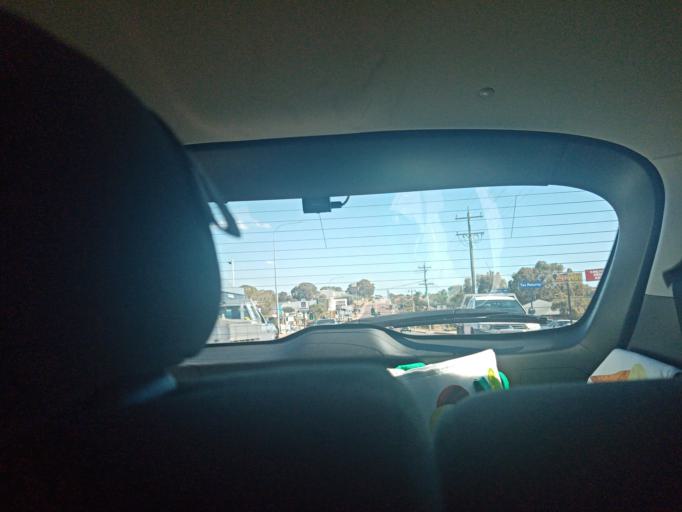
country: AU
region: Western Australia
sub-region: City of Cockburn
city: Spearwood
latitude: -32.0948
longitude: 115.7828
